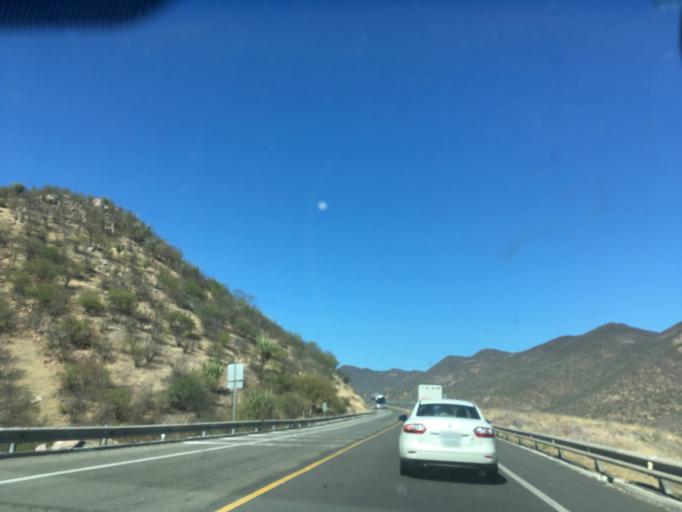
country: MX
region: Michoacan
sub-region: Arteaga
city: Las Canas
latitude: 18.4492
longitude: -101.9283
